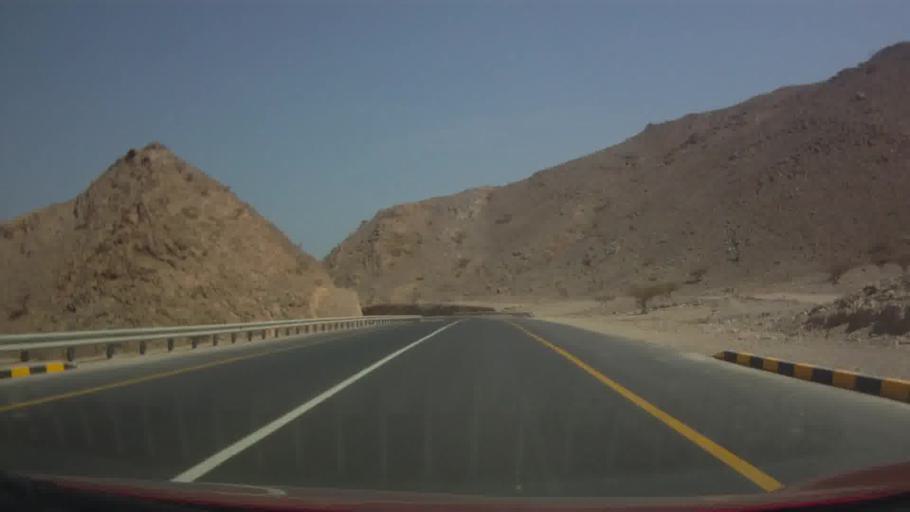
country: OM
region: Muhafazat Masqat
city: Muscat
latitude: 23.3888
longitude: 58.8023
